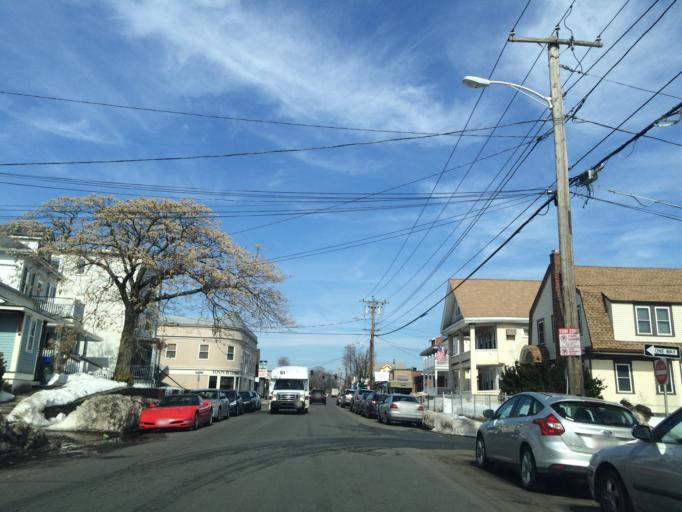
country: US
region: Massachusetts
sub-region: Middlesex County
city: Medford
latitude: 42.4038
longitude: -71.1073
